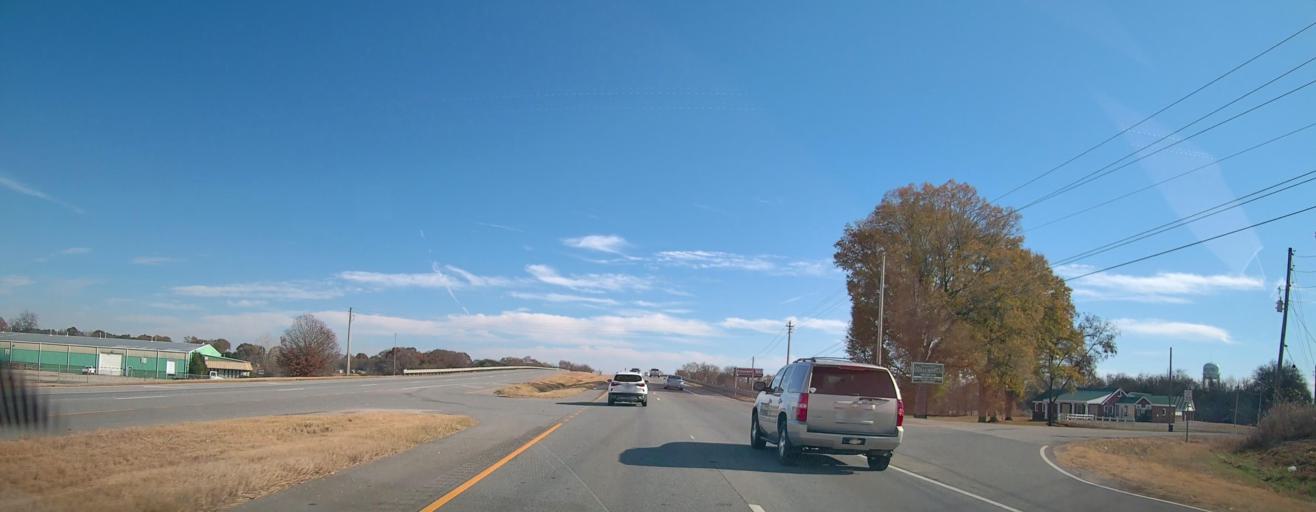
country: US
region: Alabama
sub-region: Colbert County
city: Muscle Shoals
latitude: 34.7085
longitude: -87.6614
